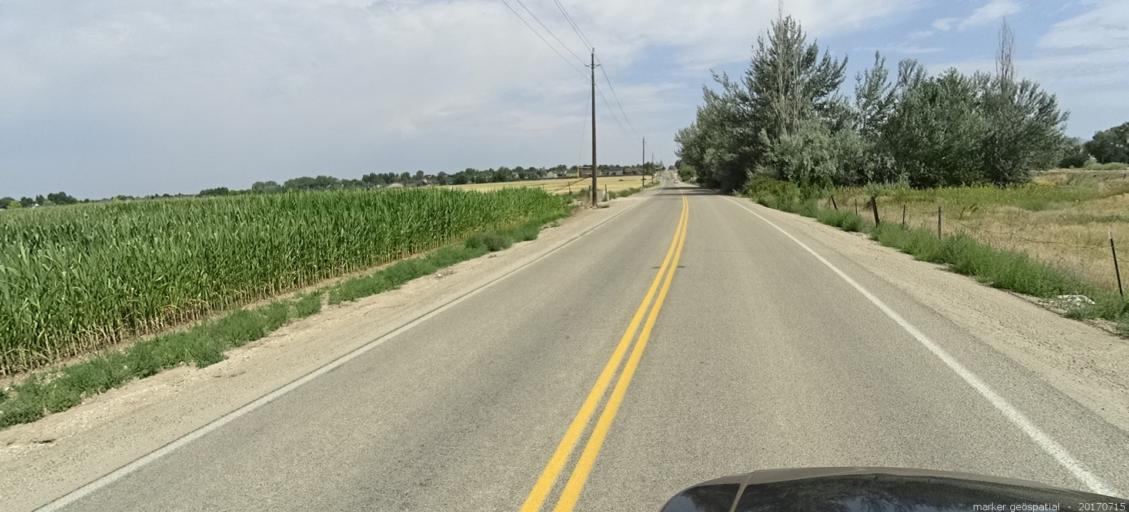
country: US
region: Idaho
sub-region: Ada County
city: Garden City
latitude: 43.5382
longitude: -116.2742
